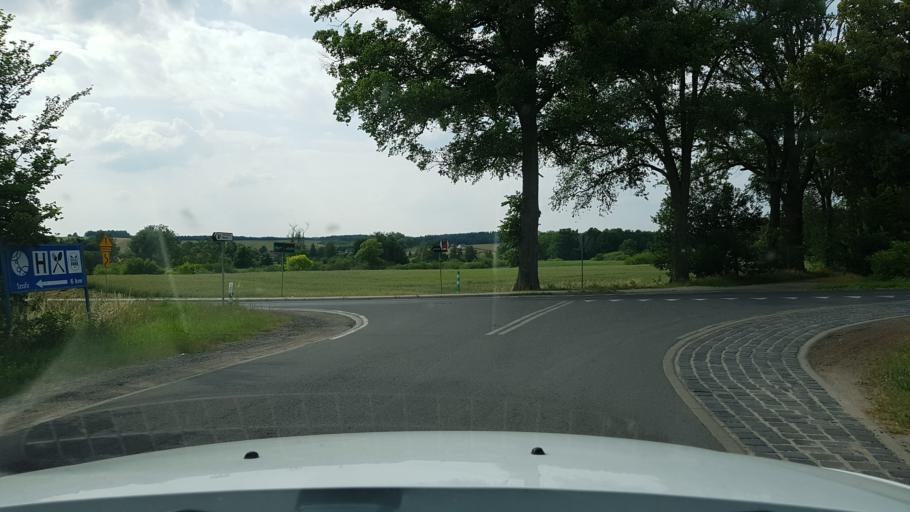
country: PL
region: West Pomeranian Voivodeship
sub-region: Powiat gryfinski
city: Moryn
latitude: 52.9164
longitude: 14.3628
